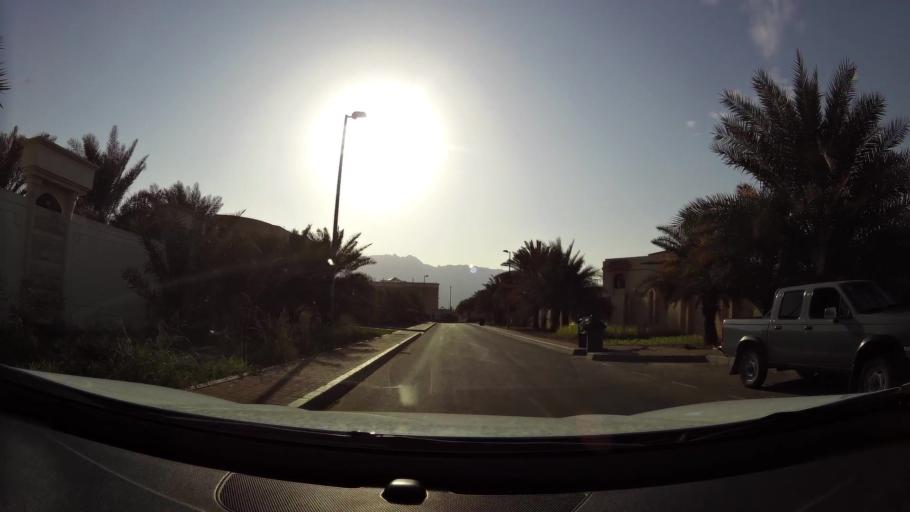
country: AE
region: Abu Dhabi
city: Al Ain
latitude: 24.0758
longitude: 55.8398
